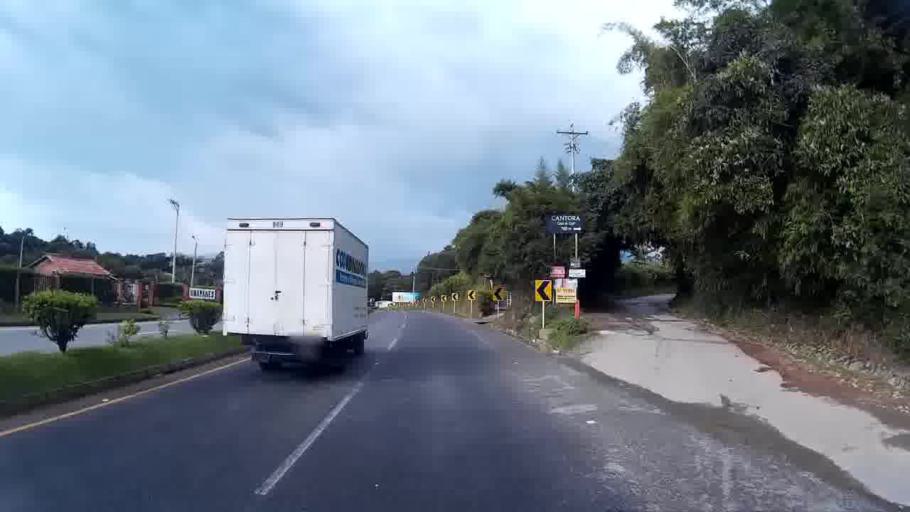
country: CO
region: Quindio
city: Circasia
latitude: 4.6257
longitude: -75.6193
